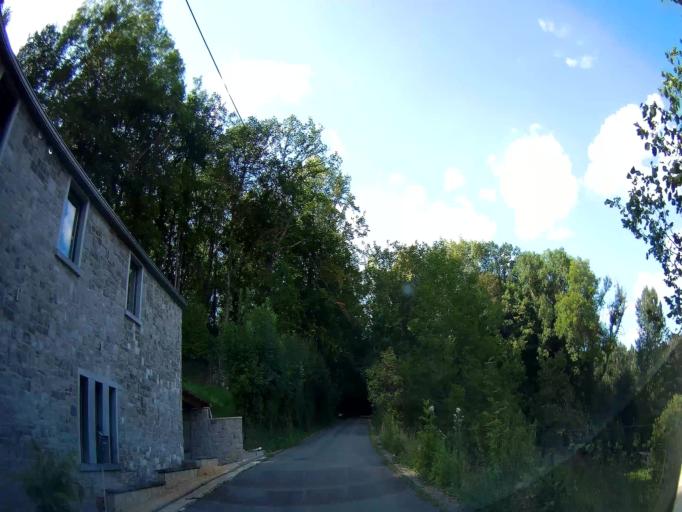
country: BE
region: Wallonia
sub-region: Province de Namur
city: Onhaye
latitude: 50.2958
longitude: 4.7773
